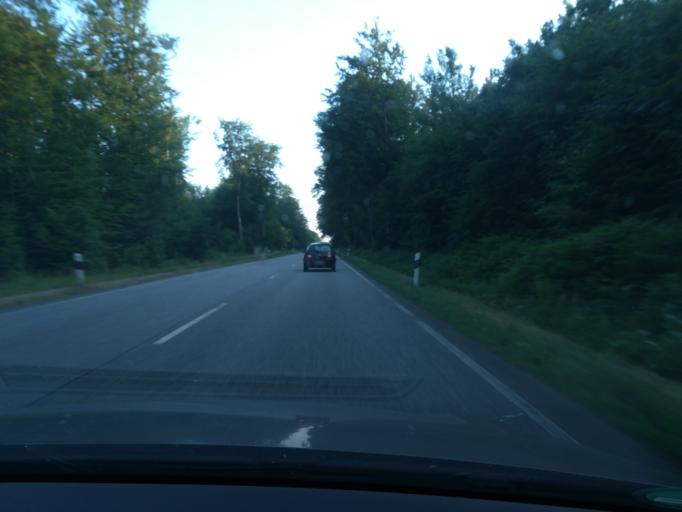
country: DE
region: Schleswig-Holstein
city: Kasseburg
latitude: 53.5446
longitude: 10.4204
